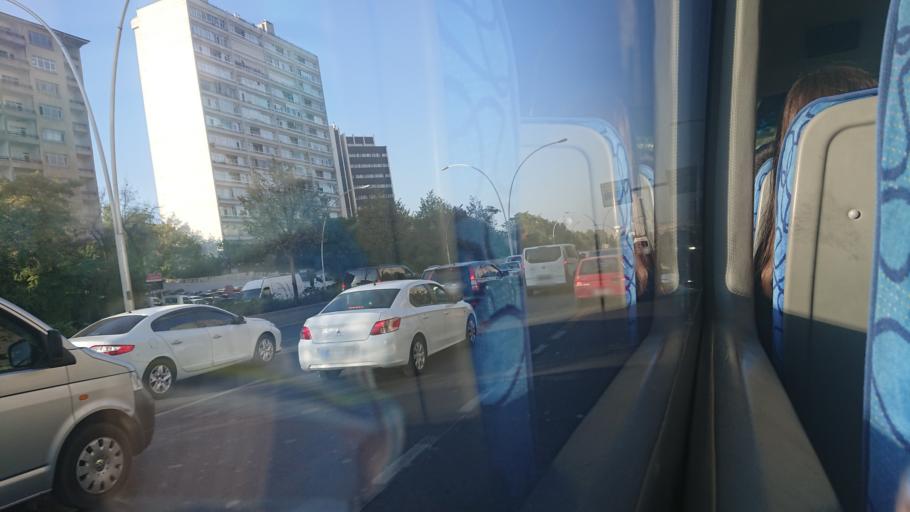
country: TR
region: Ankara
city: Ankara
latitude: 39.9288
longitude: 32.8170
